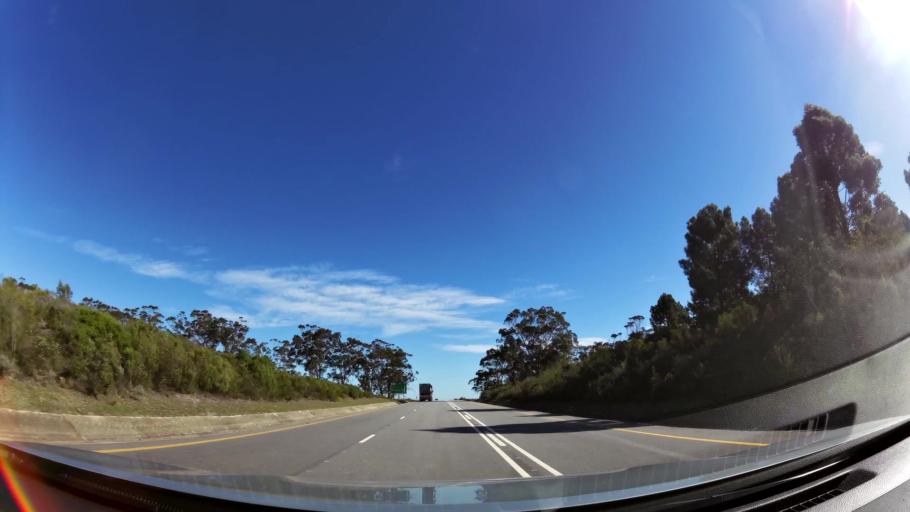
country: ZA
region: Eastern Cape
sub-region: Cacadu District Municipality
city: Kruisfontein
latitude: -34.0198
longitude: 24.6190
